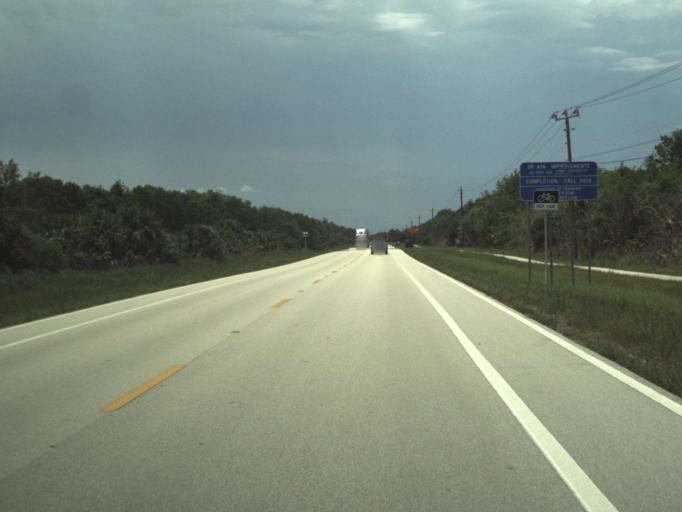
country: US
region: Florida
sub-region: Saint Lucie County
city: Hutchinson Island South
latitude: 27.3335
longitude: -80.2340
